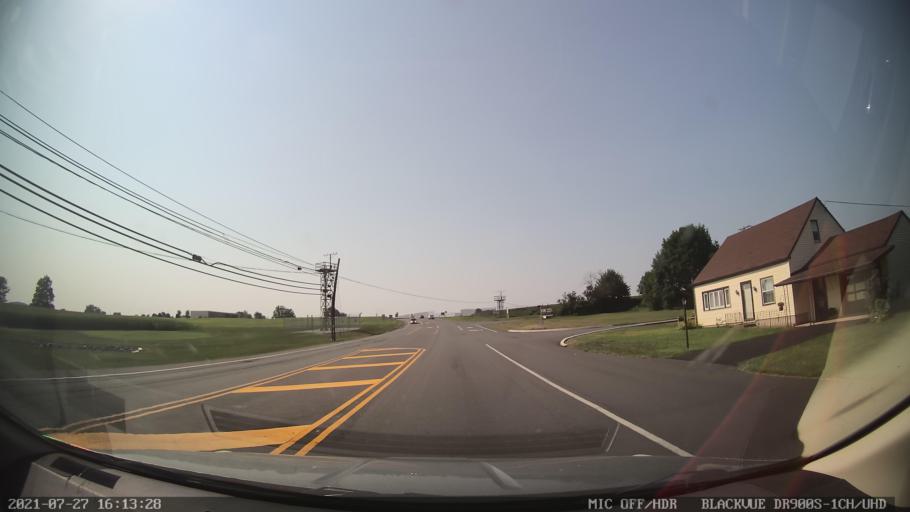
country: US
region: Pennsylvania
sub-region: Berks County
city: River View Park
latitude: 40.3686
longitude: -75.9592
